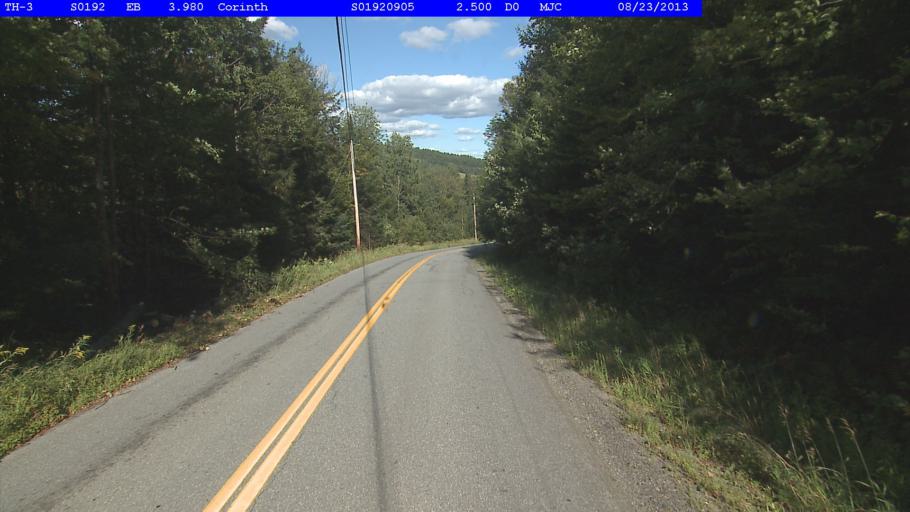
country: US
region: Vermont
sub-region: Orange County
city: Chelsea
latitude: 44.0019
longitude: -72.3103
